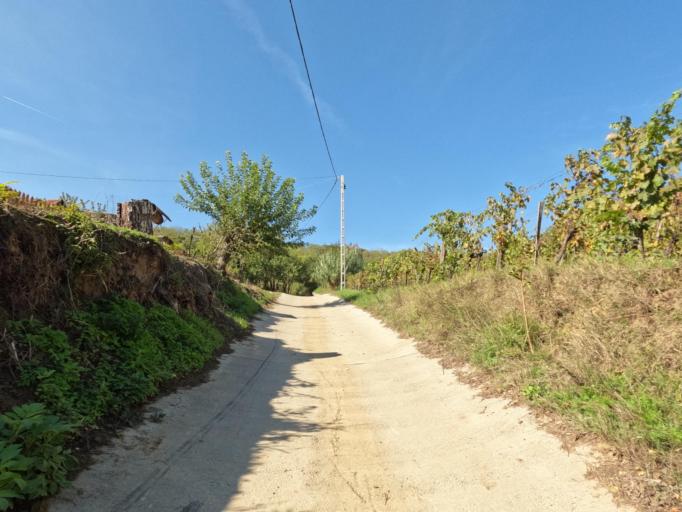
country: HU
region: Tolna
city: Szekszard
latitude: 46.3499
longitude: 18.6711
